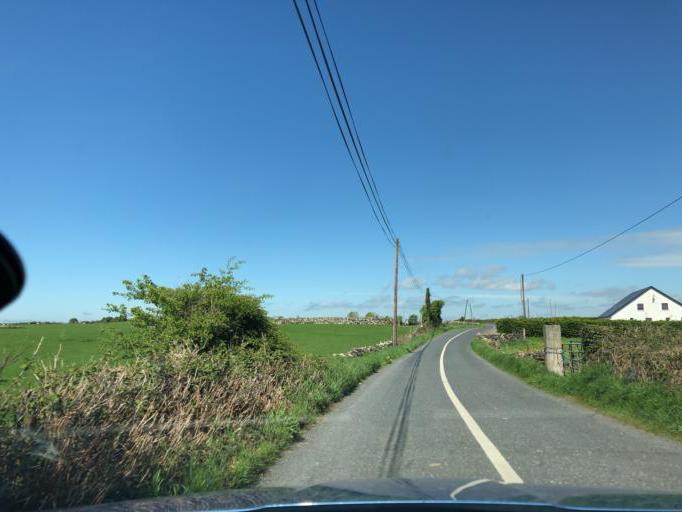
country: IE
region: Connaught
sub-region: County Galway
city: Loughrea
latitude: 53.1650
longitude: -8.4082
